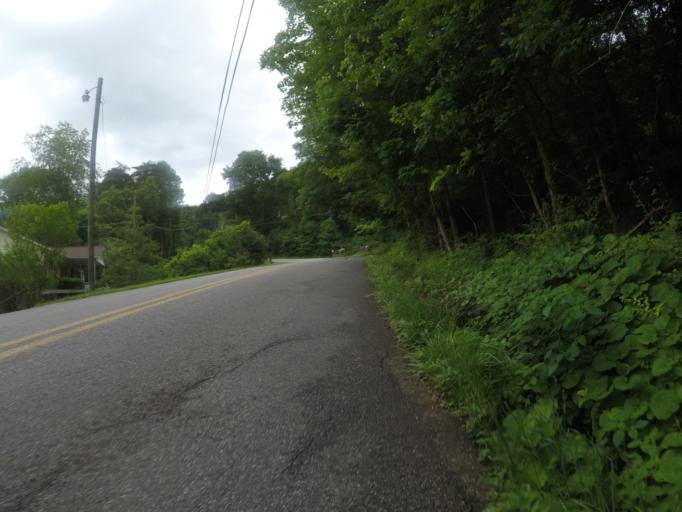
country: US
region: West Virginia
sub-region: Wayne County
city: Lavalette
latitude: 38.3645
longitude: -82.4217
